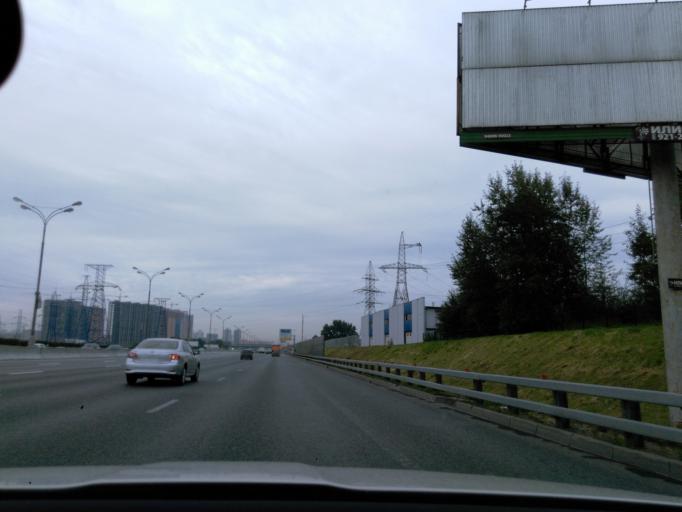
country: RU
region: Moscow
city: Ivanovskoye
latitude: 55.7847
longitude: 37.8415
